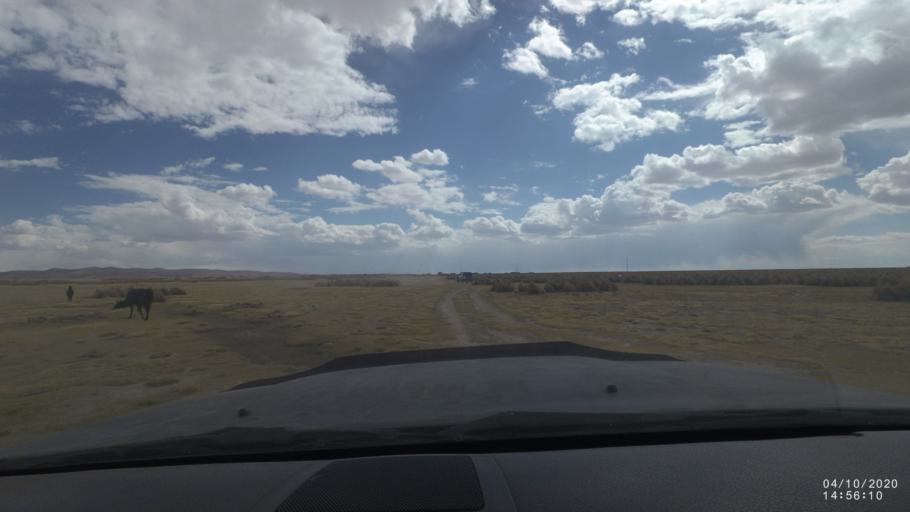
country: BO
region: Oruro
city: Poopo
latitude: -18.6842
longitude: -67.5152
